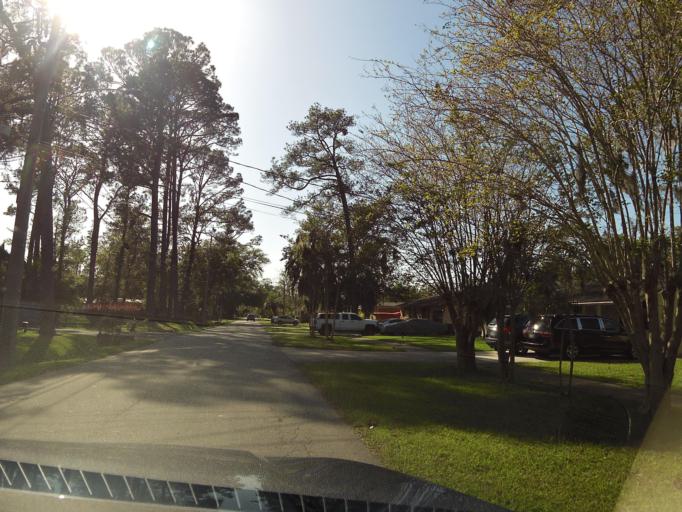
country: US
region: Florida
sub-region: Duval County
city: Jacksonville
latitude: 30.2809
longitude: -81.5974
